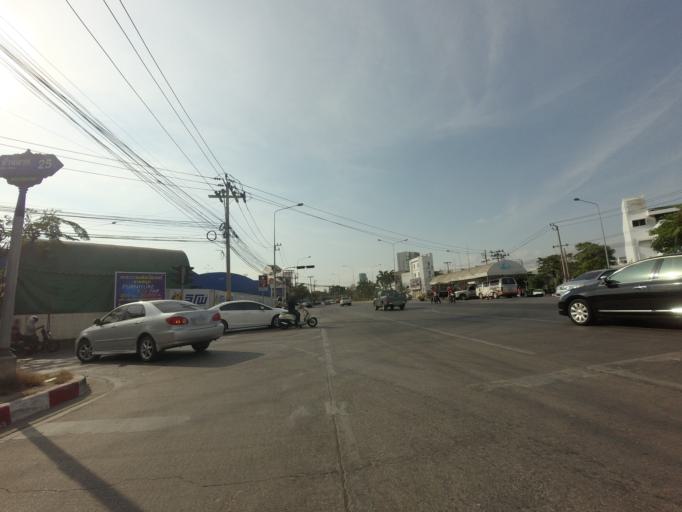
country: TH
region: Bangkok
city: Bang Kapi
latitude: 13.7539
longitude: 100.6307
